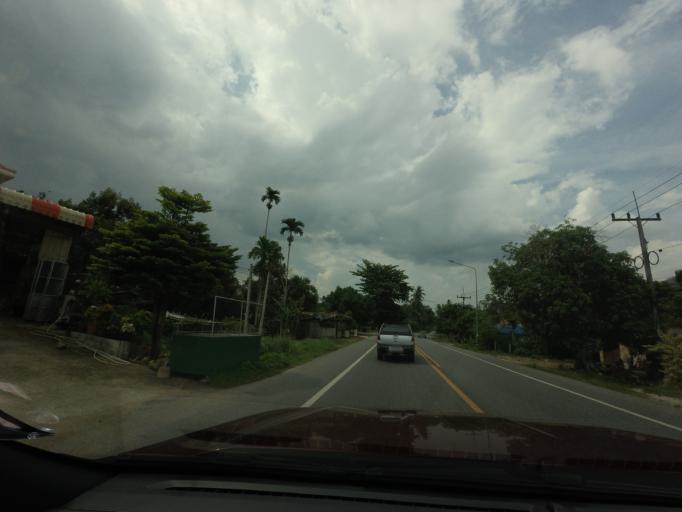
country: TH
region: Yala
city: Ban Nang Sata
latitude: 6.2741
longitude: 101.2840
